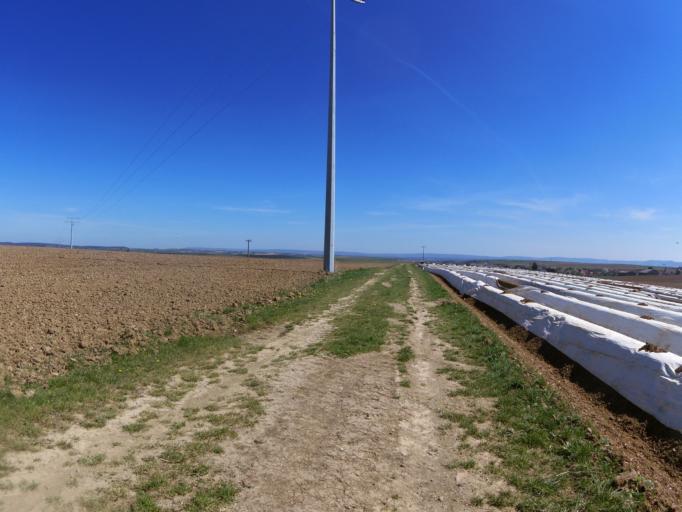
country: DE
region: Bavaria
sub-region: Regierungsbezirk Unterfranken
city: Biebelried
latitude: 49.8009
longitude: 10.0933
